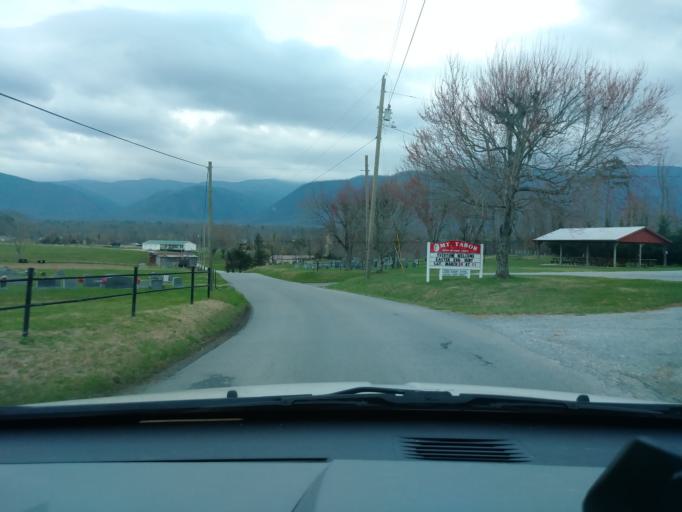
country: US
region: Tennessee
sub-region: Greene County
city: Tusculum
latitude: 36.0887
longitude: -82.7477
